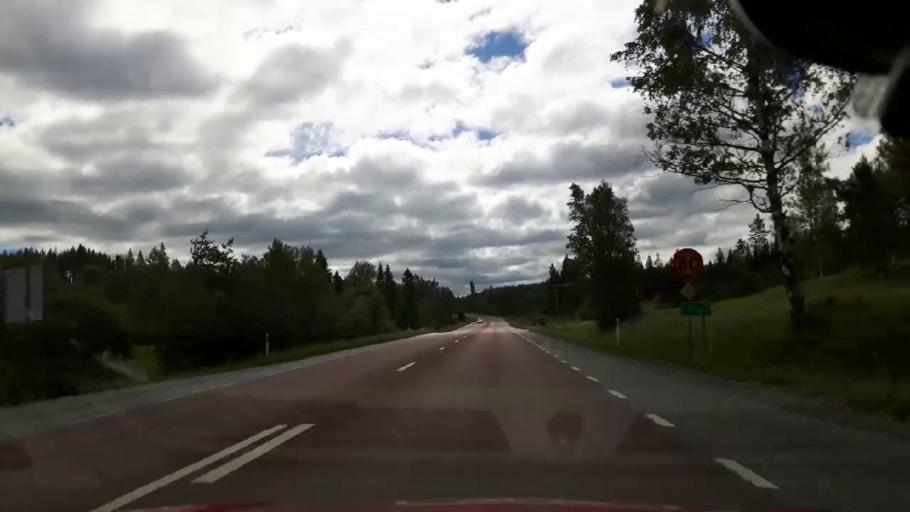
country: SE
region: Jaemtland
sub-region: Braecke Kommun
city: Braecke
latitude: 62.9505
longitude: 15.1622
